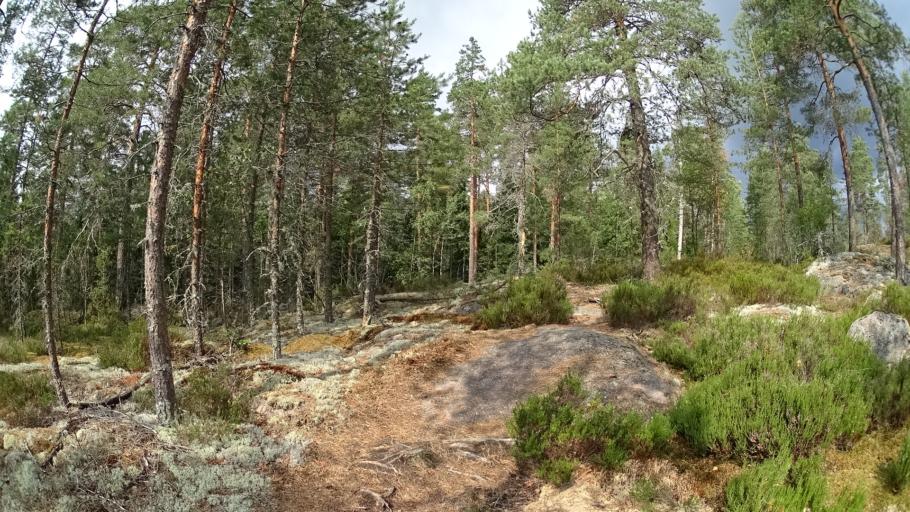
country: FI
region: Uusimaa
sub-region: Helsinki
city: Espoo
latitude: 60.3023
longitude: 24.5820
